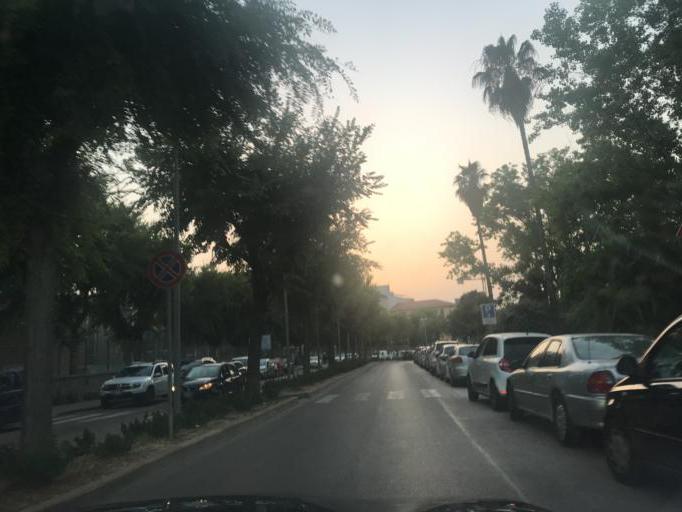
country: IT
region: Sardinia
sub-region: Provincia di Sassari
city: Alghero
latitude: 40.5554
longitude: 8.3195
